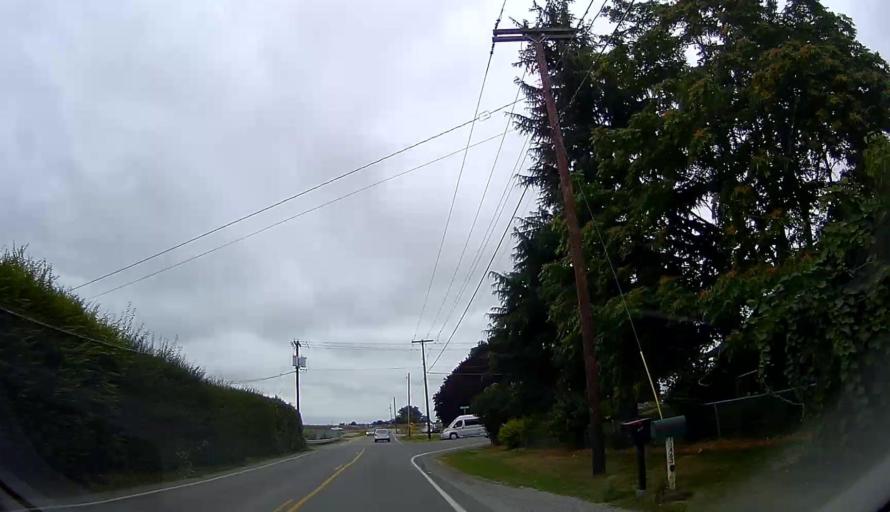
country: US
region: Washington
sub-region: Skagit County
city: Mount Vernon
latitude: 48.4508
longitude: -122.3571
